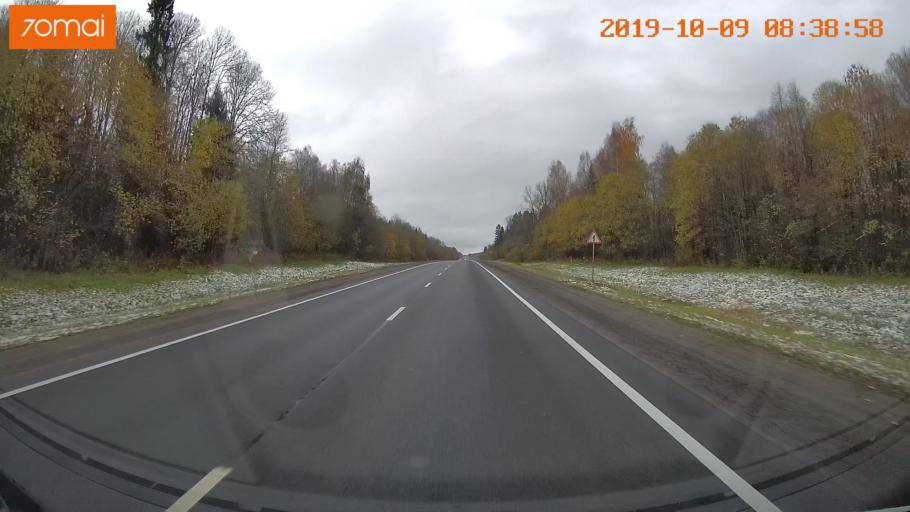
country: RU
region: Vologda
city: Gryazovets
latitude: 58.9644
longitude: 40.1590
